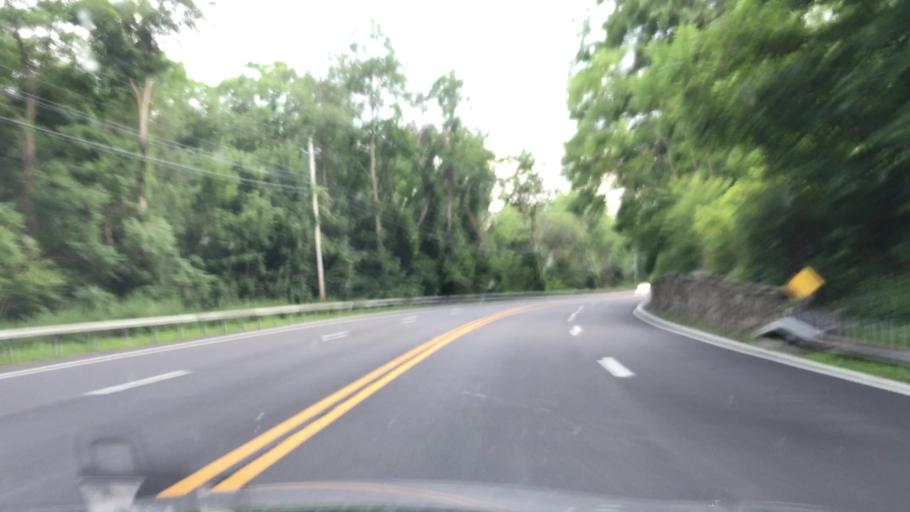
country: US
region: New York
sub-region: Orange County
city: Harriman
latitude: 41.2740
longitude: -74.1533
